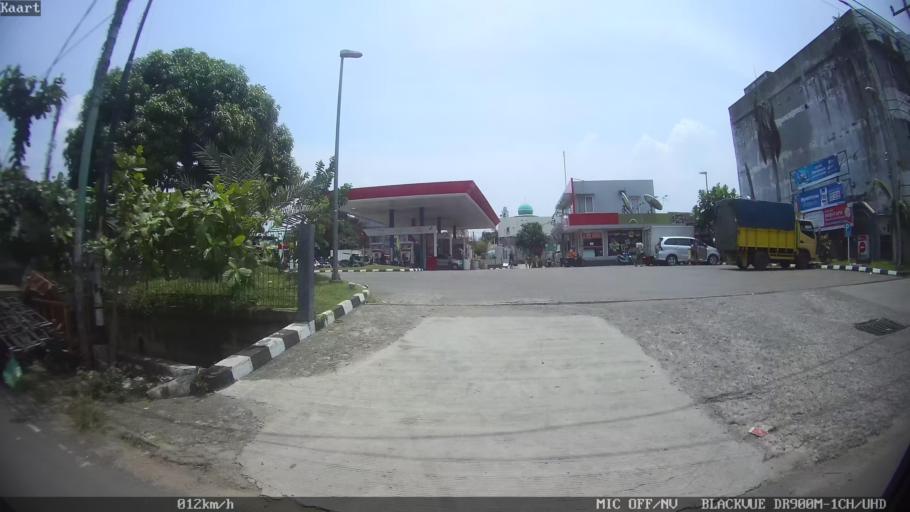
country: ID
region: Lampung
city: Bandarlampung
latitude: -5.4451
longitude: 105.2699
